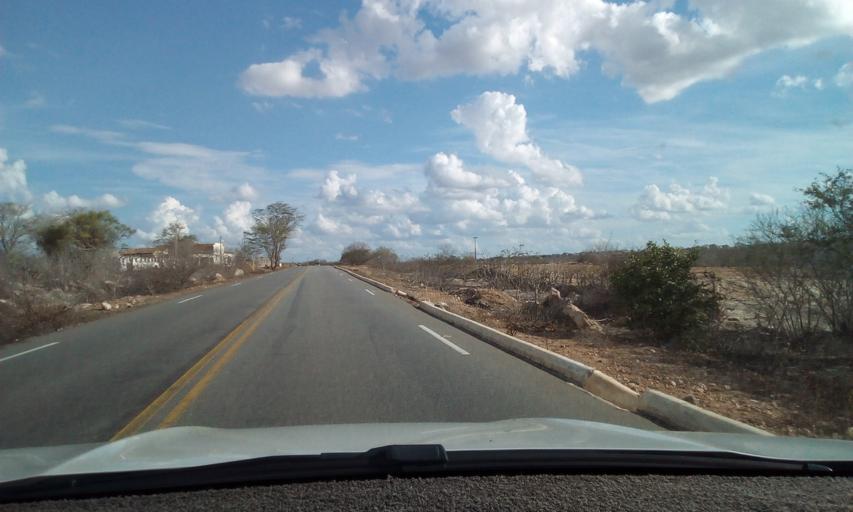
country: BR
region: Paraiba
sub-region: Soledade
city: Soledade
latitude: -6.9061
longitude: -36.3884
